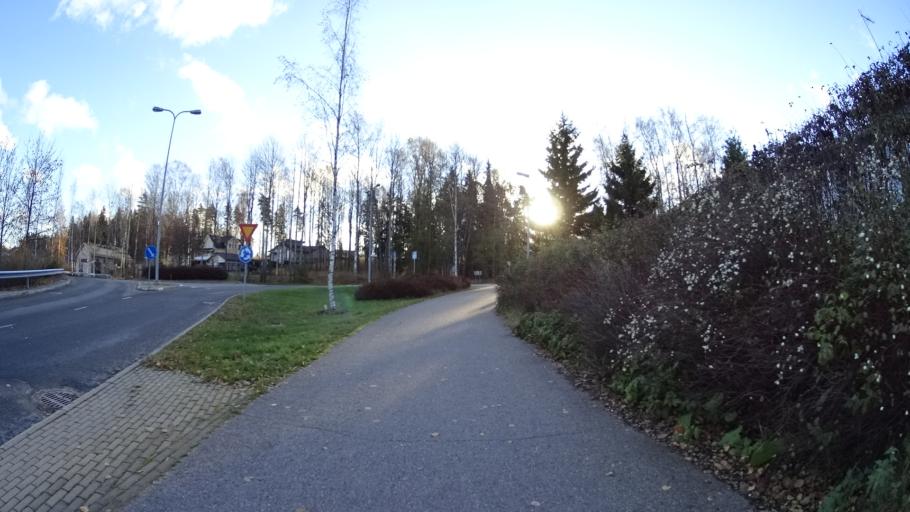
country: FI
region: Uusimaa
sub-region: Helsinki
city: Kilo
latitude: 60.2482
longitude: 24.8073
